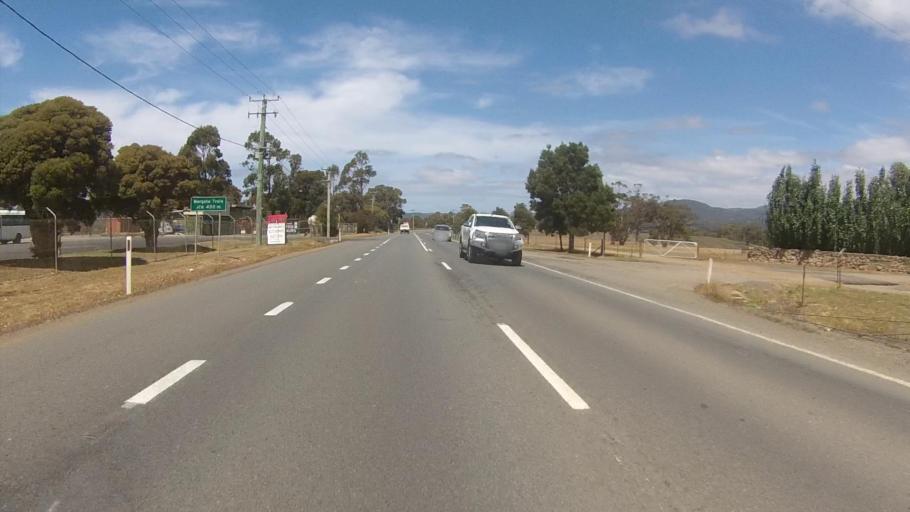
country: AU
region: Tasmania
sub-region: Kingborough
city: Margate
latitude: -43.0138
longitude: 147.2718
